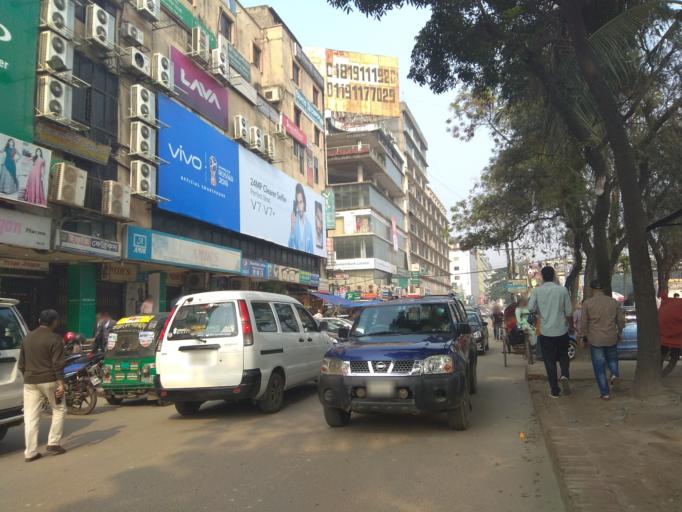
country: BD
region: Dhaka
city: Tungi
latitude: 23.8641
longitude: 90.3999
